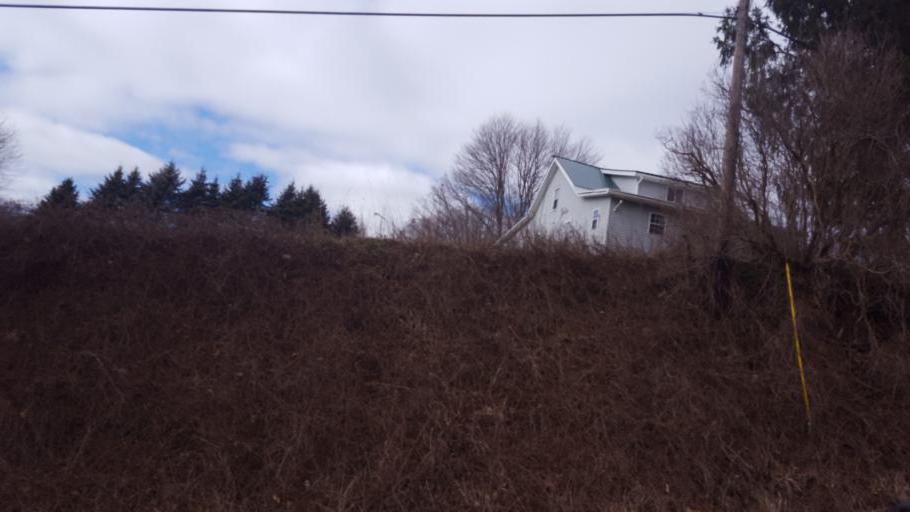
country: US
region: Ohio
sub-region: Sandusky County
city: Bellville
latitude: 40.6728
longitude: -82.5113
